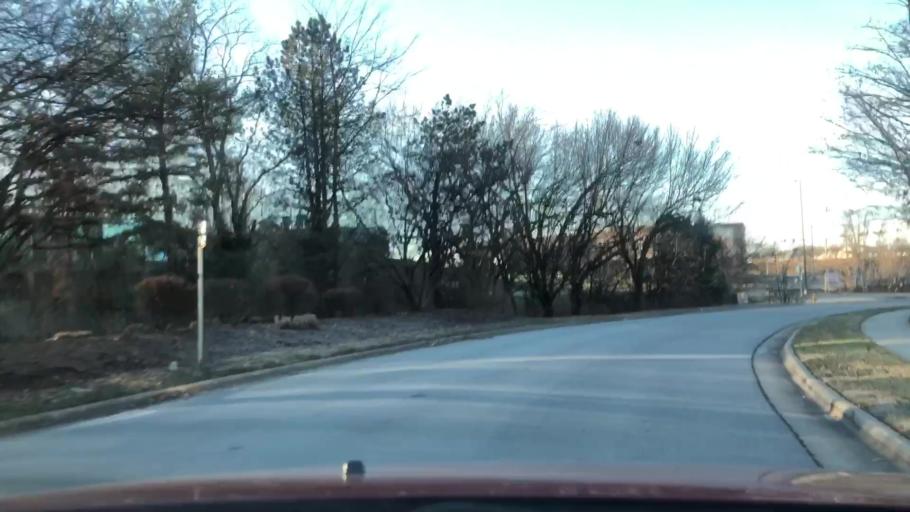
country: US
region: Missouri
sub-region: Greene County
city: Springfield
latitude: 37.1449
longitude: -93.2764
